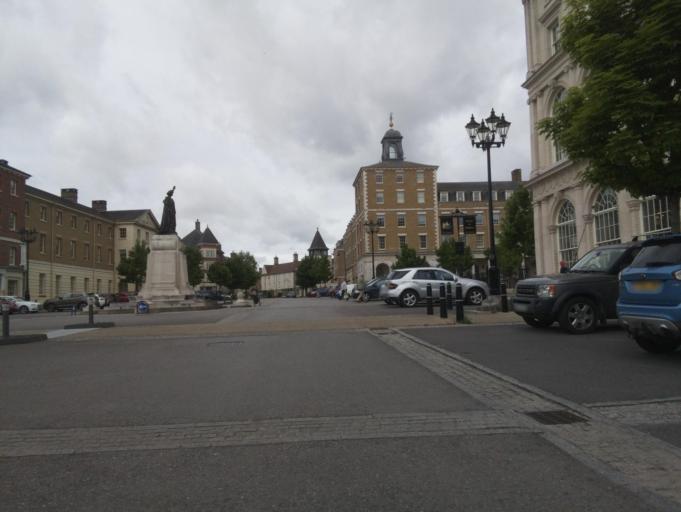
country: GB
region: England
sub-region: Dorset
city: Dorchester
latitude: 50.7150
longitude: -2.4655
